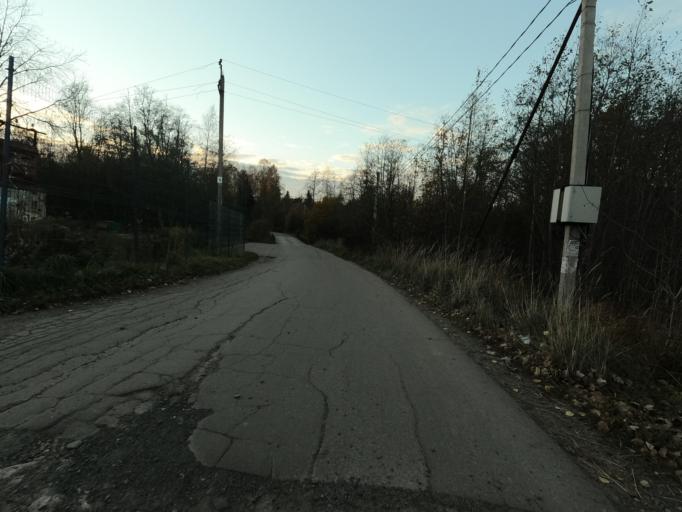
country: RU
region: Leningrad
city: Mga
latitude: 59.7811
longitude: 31.2026
